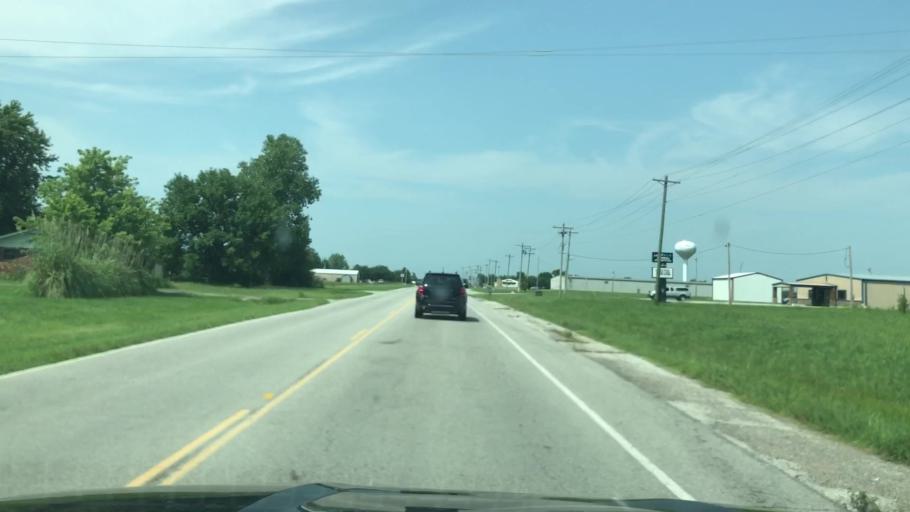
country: US
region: Oklahoma
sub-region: Ottawa County
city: Commerce
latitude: 36.9075
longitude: -94.8420
